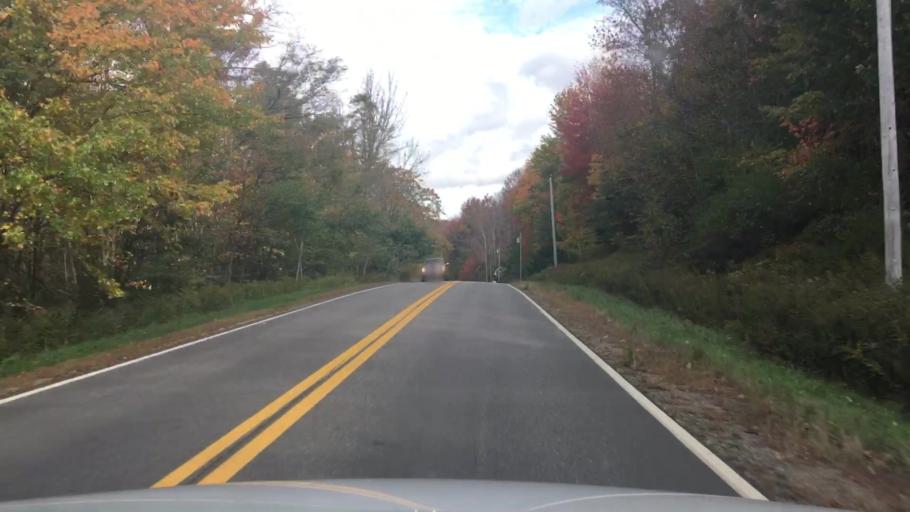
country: US
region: Maine
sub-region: Waldo County
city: Searsmont
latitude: 44.3383
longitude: -69.1388
